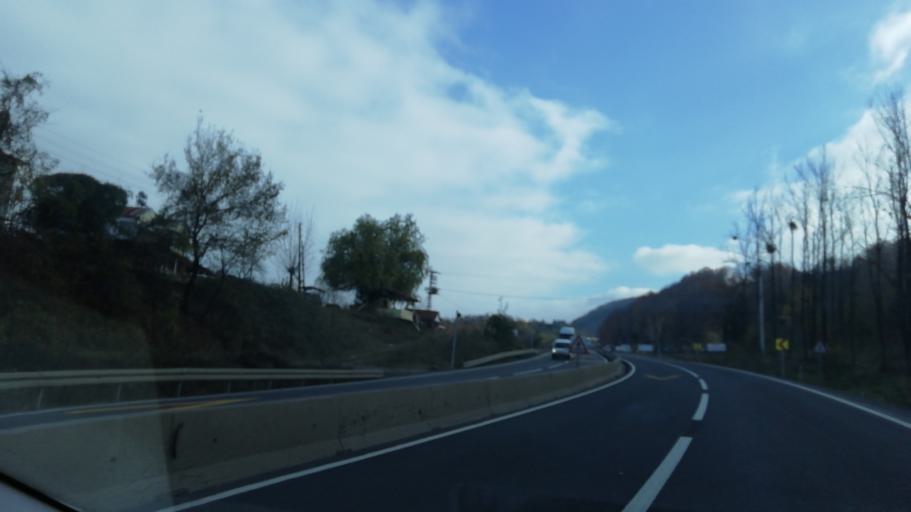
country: TR
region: Duzce
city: Kaynasli
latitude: 40.7584
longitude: 31.3514
